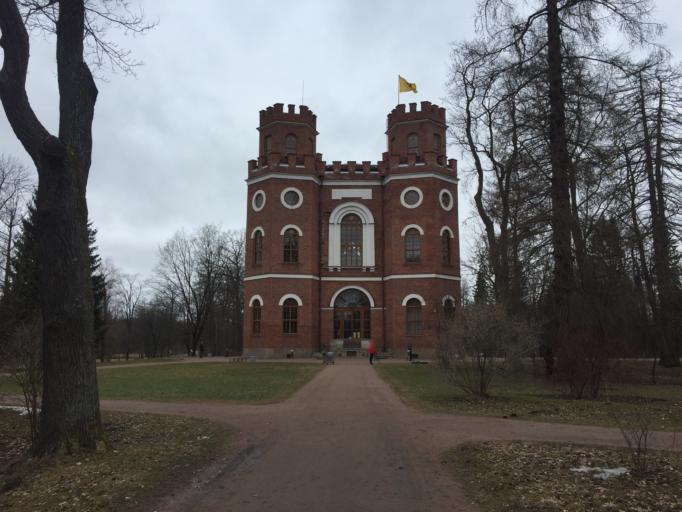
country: RU
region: St.-Petersburg
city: Pushkin
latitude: 59.7215
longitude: 30.3784
